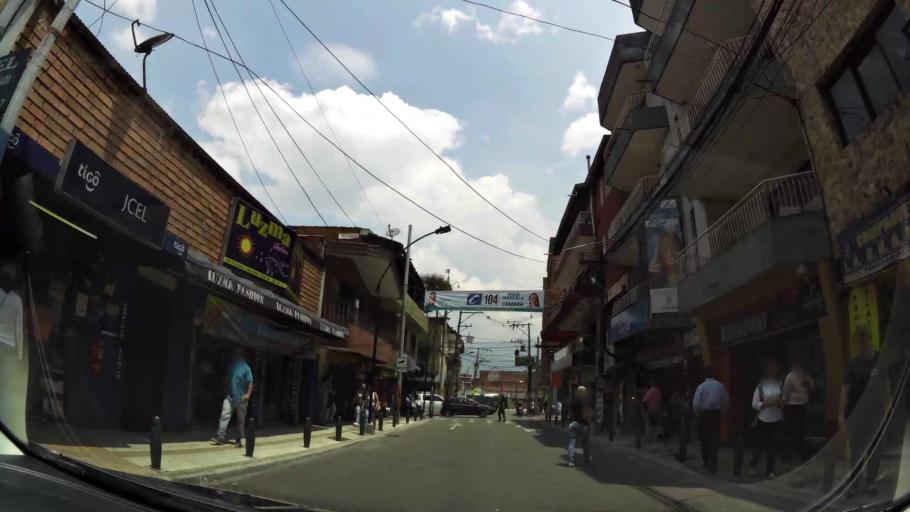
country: CO
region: Antioquia
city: Itagui
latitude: 6.1724
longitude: -75.6084
